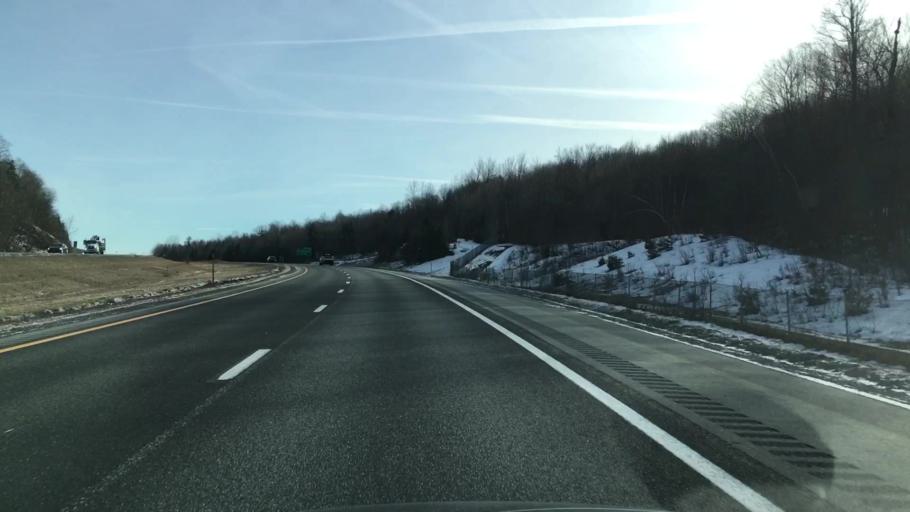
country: US
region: New Hampshire
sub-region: Grafton County
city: Enfield
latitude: 43.5747
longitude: -72.1602
